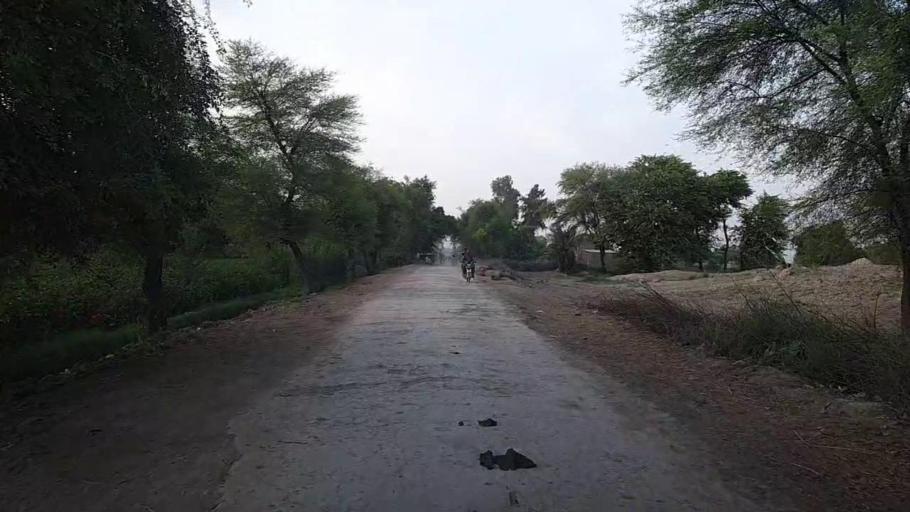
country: PK
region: Sindh
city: Ubauro
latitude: 28.2920
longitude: 69.7996
